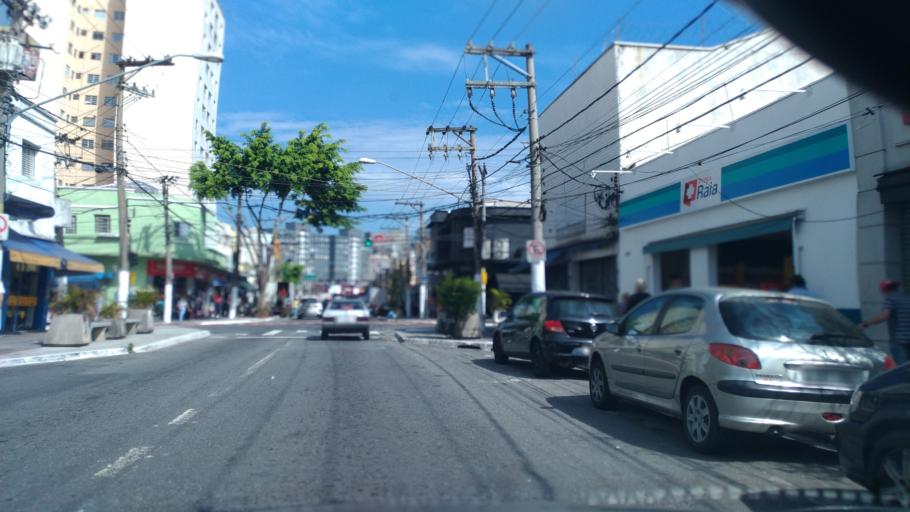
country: BR
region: Sao Paulo
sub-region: Sao Caetano Do Sul
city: Sao Caetano do Sul
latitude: -23.5987
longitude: -46.6006
